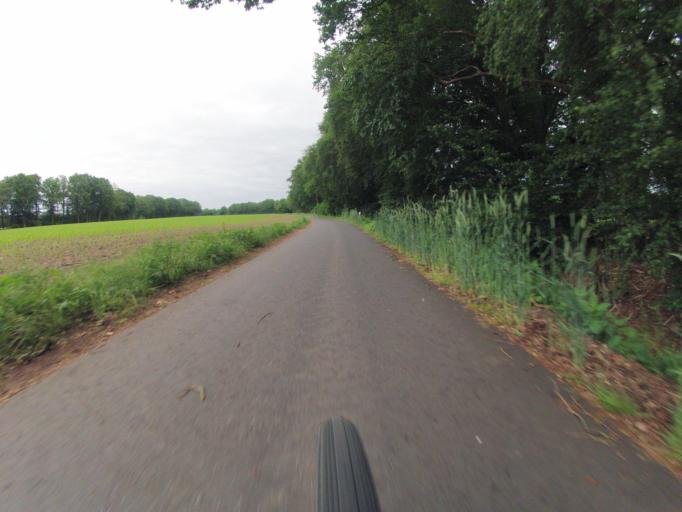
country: DE
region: North Rhine-Westphalia
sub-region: Regierungsbezirk Munster
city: Horstel
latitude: 52.2432
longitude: 7.5468
